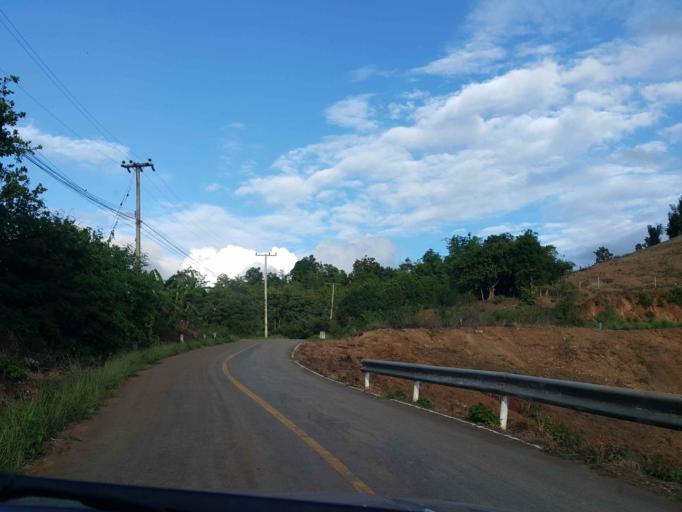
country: TH
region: Chiang Mai
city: Mae Chaem
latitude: 18.5128
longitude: 98.4036
